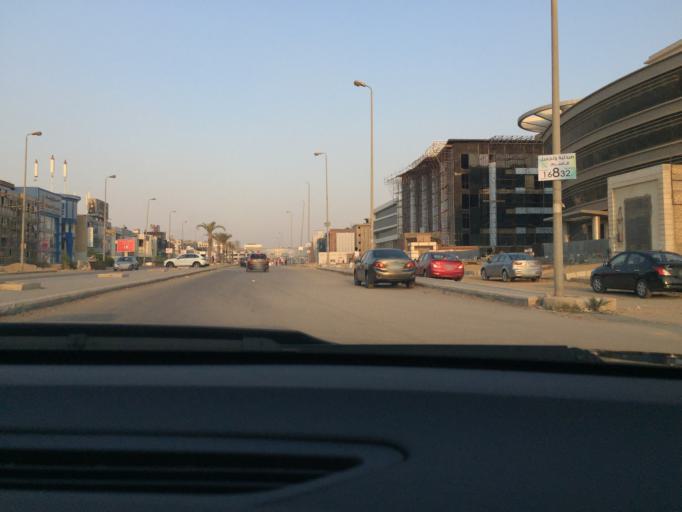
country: EG
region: Muhafazat al Qahirah
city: Cairo
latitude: 30.0183
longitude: 31.4184
